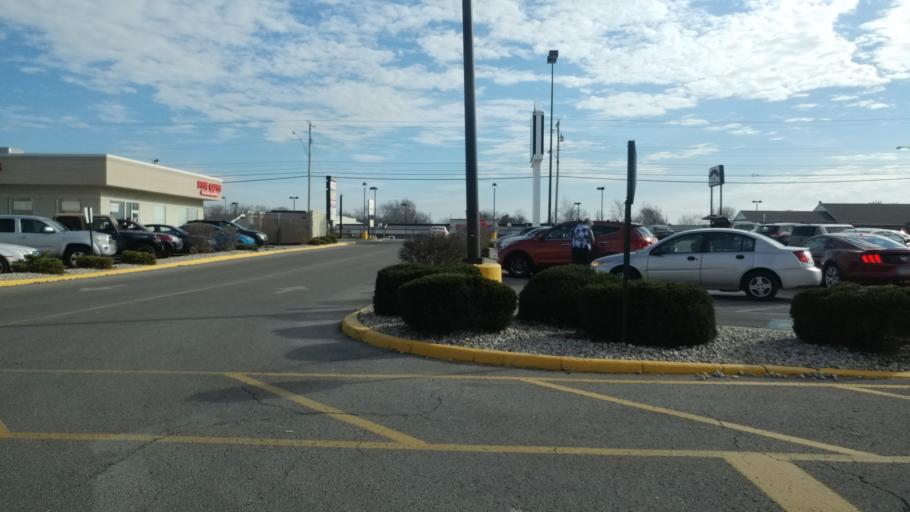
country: US
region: Ohio
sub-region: Hancock County
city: Findlay
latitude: 41.0536
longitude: -83.6151
